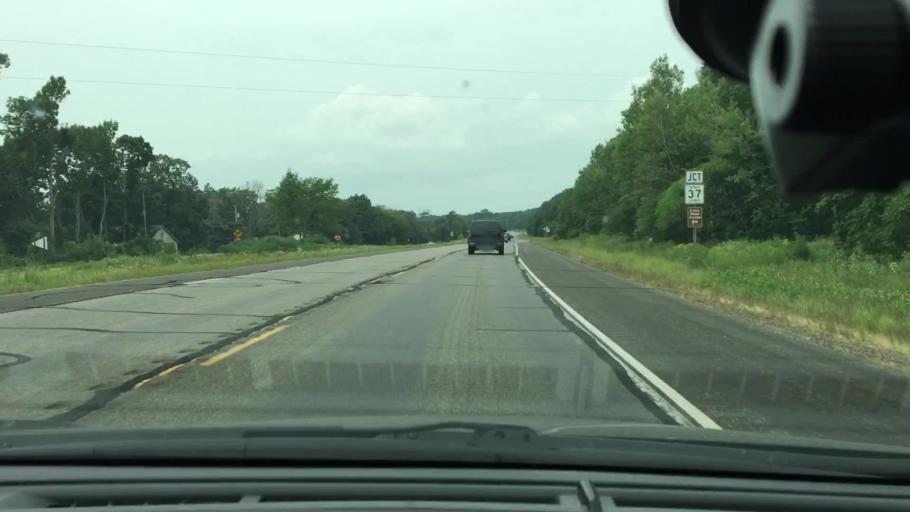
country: US
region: Minnesota
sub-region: Mille Lacs County
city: Vineland
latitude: 46.3272
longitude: -93.7747
